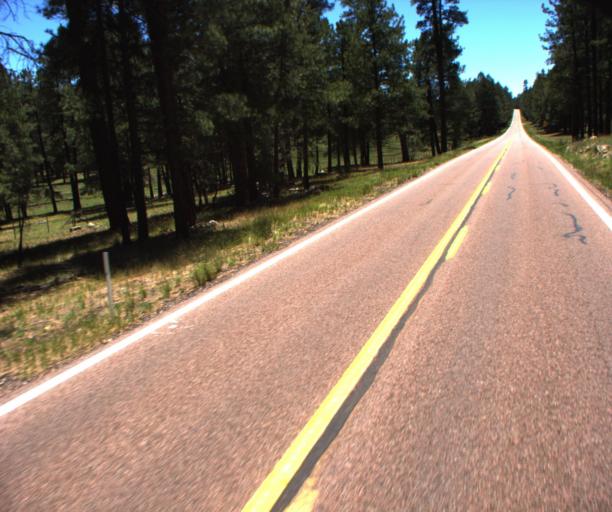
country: US
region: Arizona
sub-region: Gila County
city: Pine
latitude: 34.5281
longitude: -111.3418
